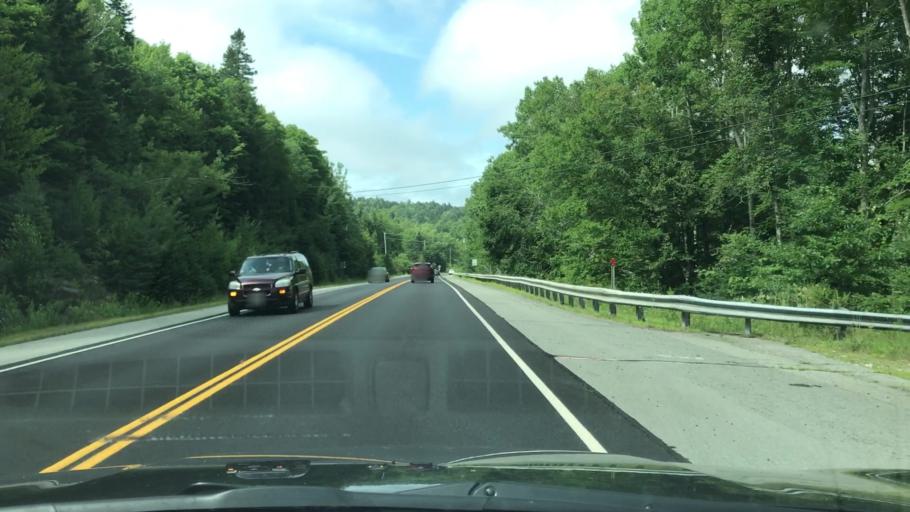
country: US
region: Maine
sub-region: Hancock County
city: Bucksport
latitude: 44.5514
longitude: -68.8098
